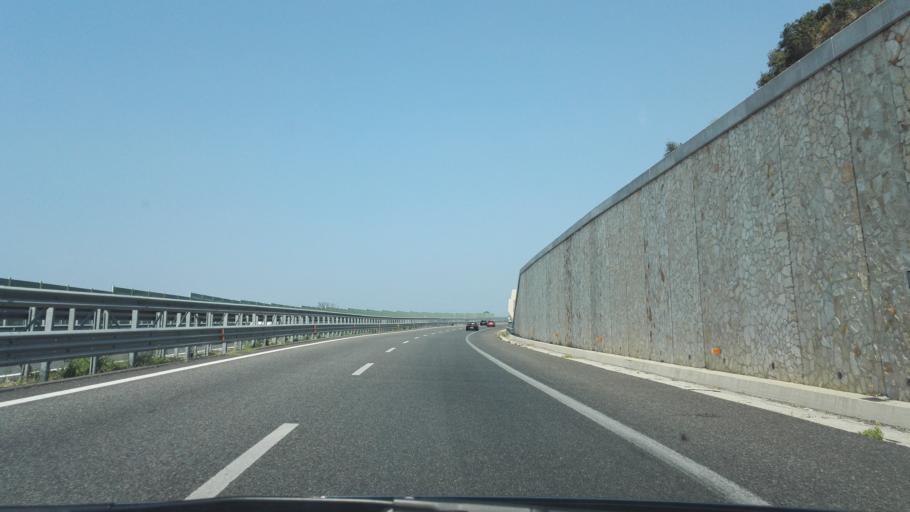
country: IT
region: Calabria
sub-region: Provincia di Catanzaro
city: Nocera Scalo
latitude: 39.0096
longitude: 16.1289
